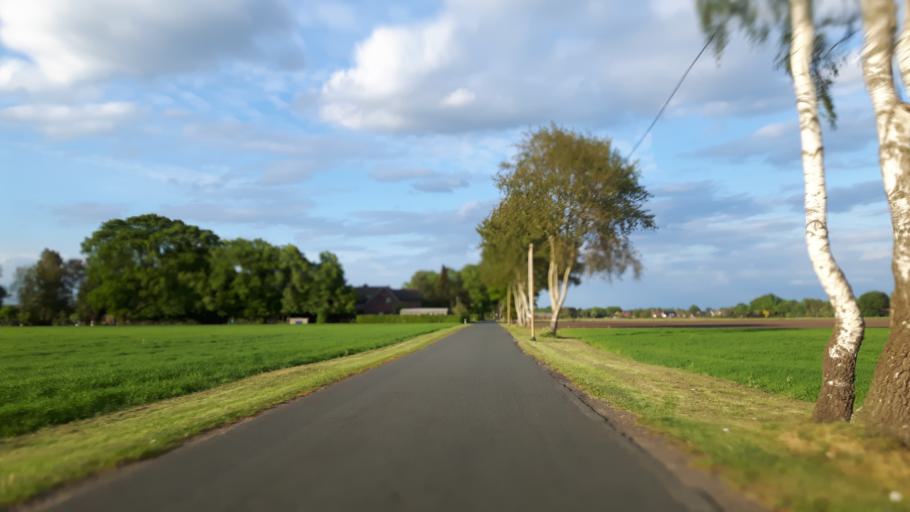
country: DE
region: Lower Saxony
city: Delmenhorst
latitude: 53.0257
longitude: 8.6042
